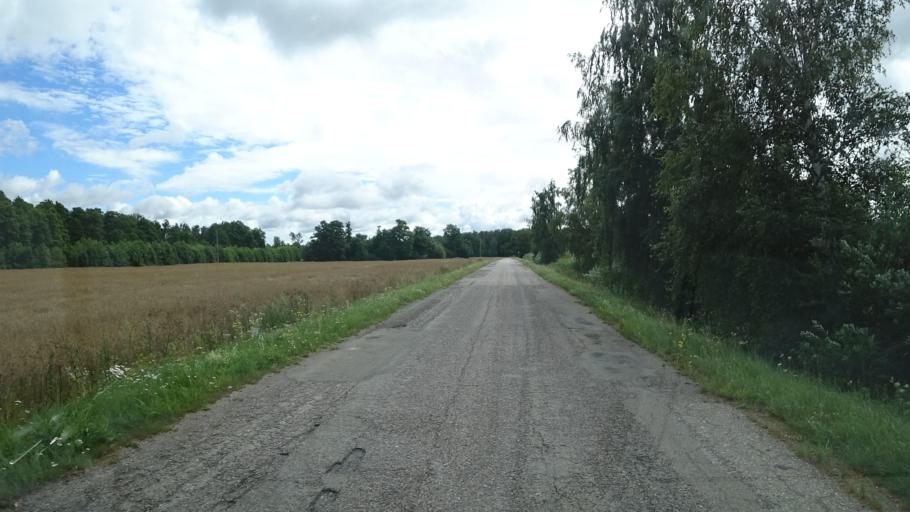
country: LV
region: Liepaja
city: Vec-Liepaja
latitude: 56.6587
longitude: 21.0855
